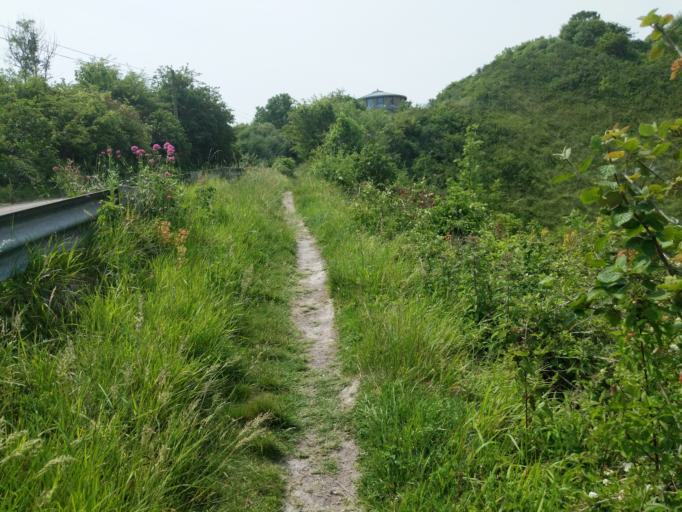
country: GB
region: England
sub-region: Kent
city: Folkestone
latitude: 51.0920
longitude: 1.2005
